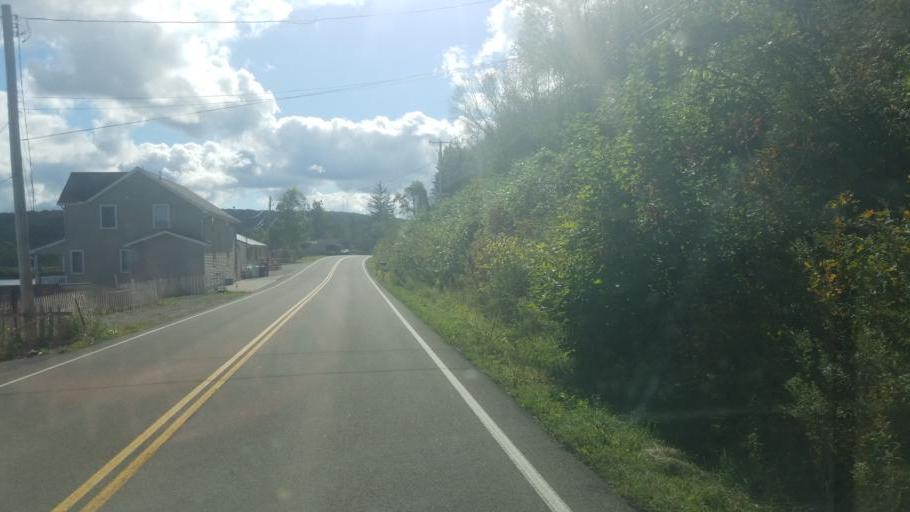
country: US
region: New York
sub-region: Allegany County
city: Cuba
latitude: 42.2460
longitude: -78.2797
